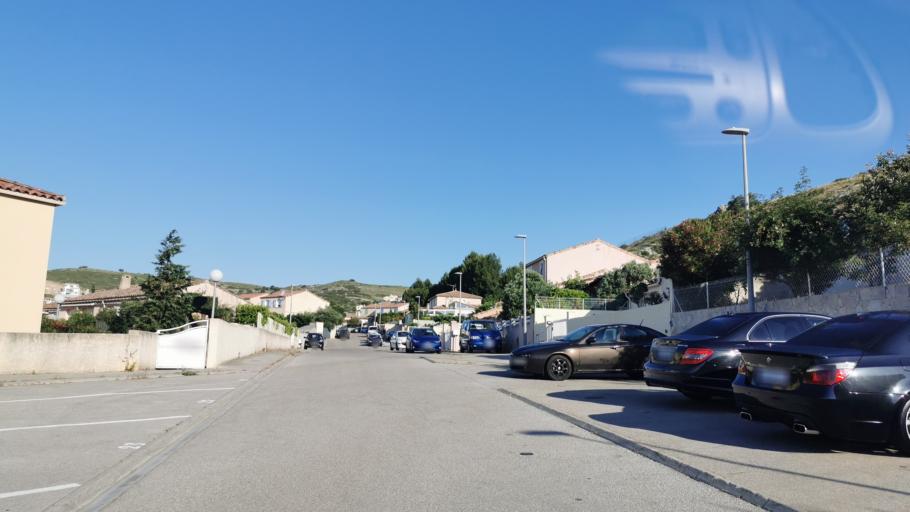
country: FR
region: Languedoc-Roussillon
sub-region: Departement de l'Aude
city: Narbonne
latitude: 43.1616
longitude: 2.9724
